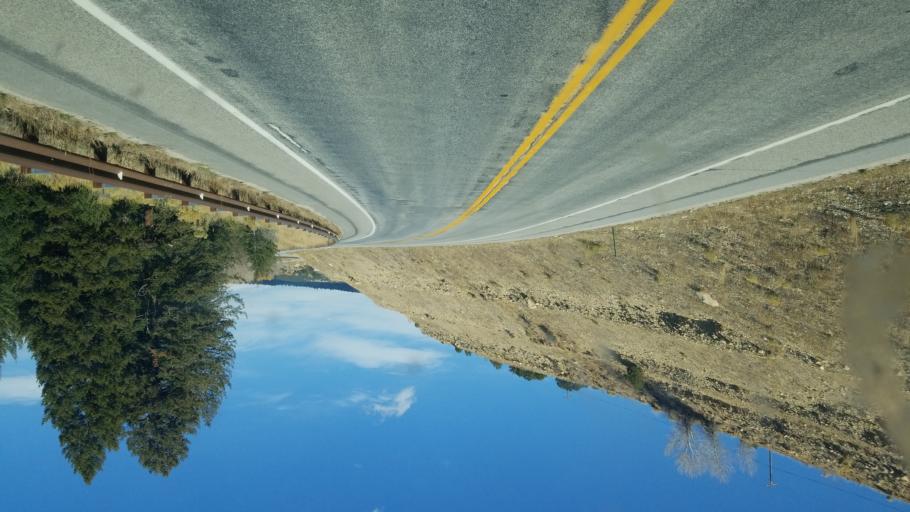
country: US
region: Colorado
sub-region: Chaffee County
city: Buena Vista
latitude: 38.9037
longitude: -106.1749
